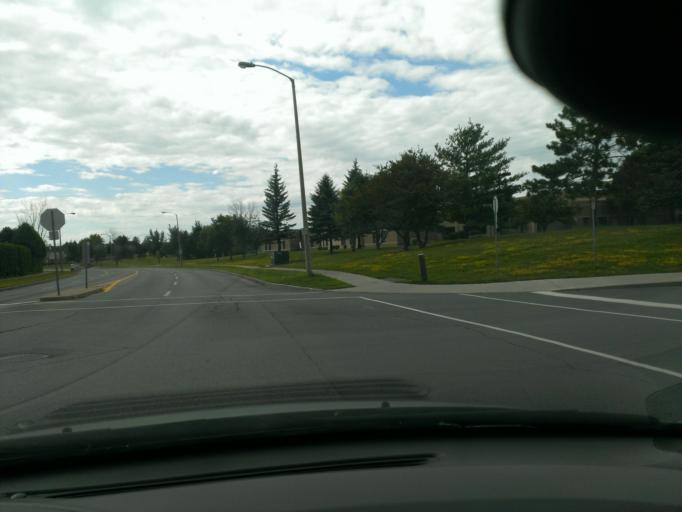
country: CA
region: Ontario
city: Clarence-Rockland
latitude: 45.4778
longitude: -75.4797
